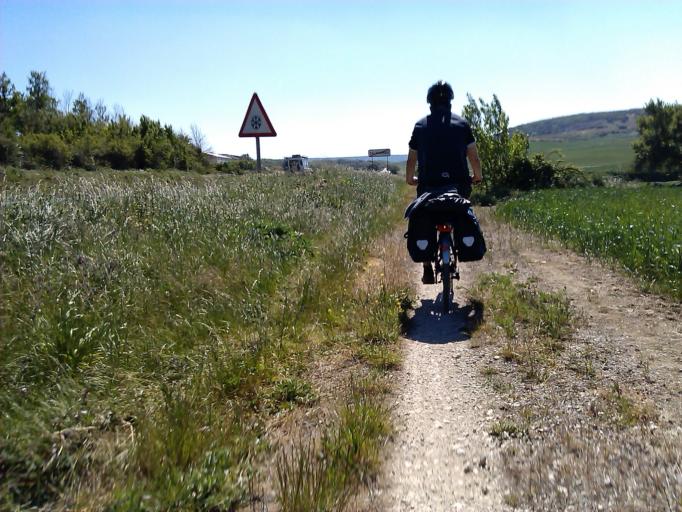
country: ES
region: Castille and Leon
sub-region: Provincia de Burgos
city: Atapuerca
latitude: 42.3465
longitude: -3.4877
